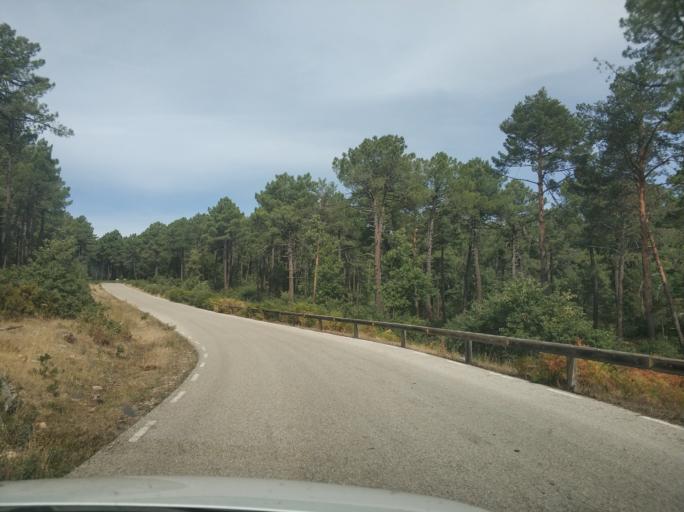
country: ES
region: Castille and Leon
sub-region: Provincia de Soria
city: Duruelo de la Sierra
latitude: 41.8906
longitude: -2.9417
